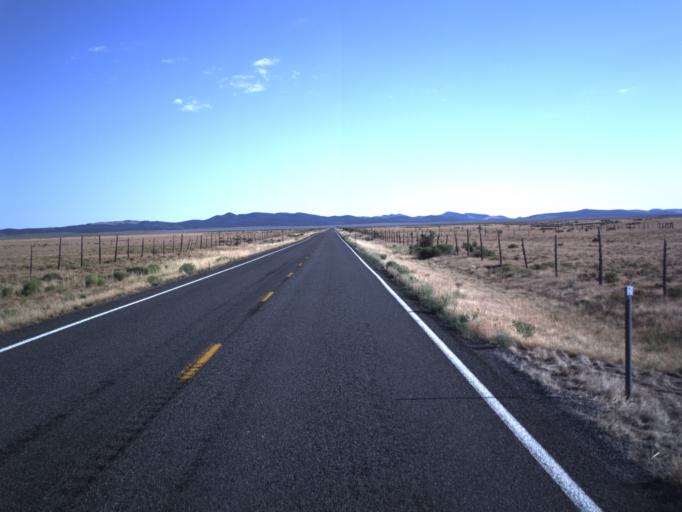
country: US
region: Utah
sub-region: Iron County
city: Enoch
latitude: 37.8955
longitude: -113.0315
